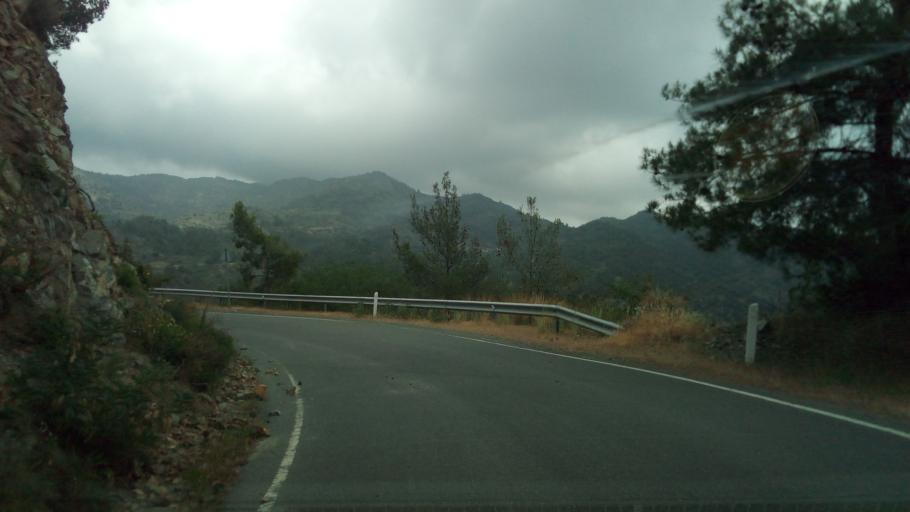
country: CY
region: Limassol
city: Pelendri
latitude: 34.8934
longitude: 32.9959
